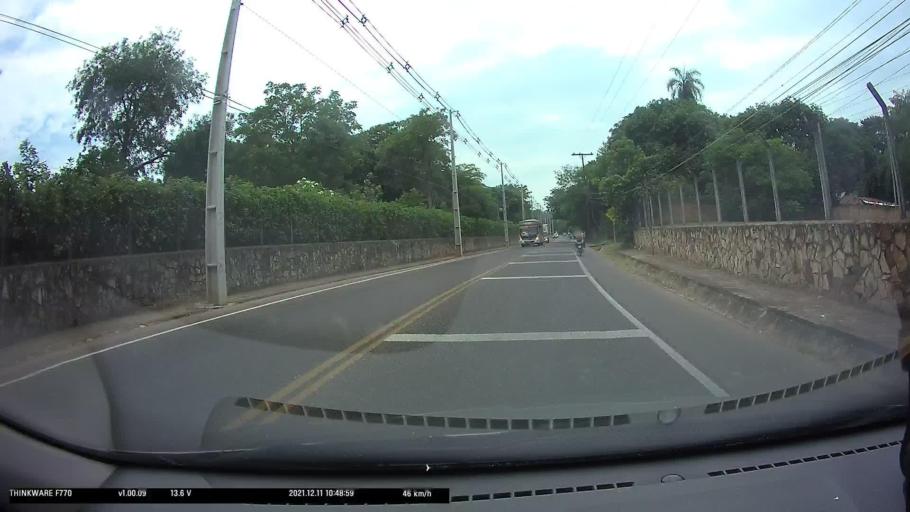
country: PY
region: Cordillera
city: San Bernardino
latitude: -25.2971
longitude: -57.2838
